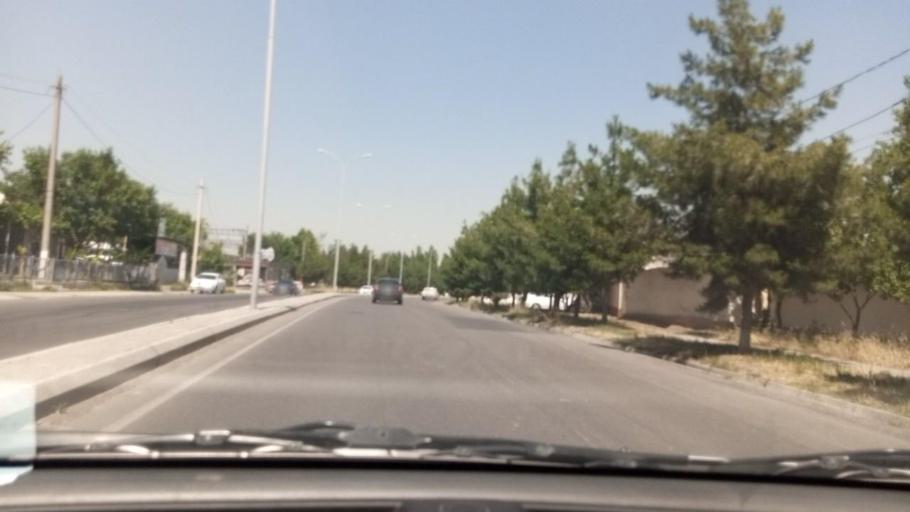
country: UZ
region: Toshkent Shahri
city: Tashkent
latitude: 41.2458
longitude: 69.2040
